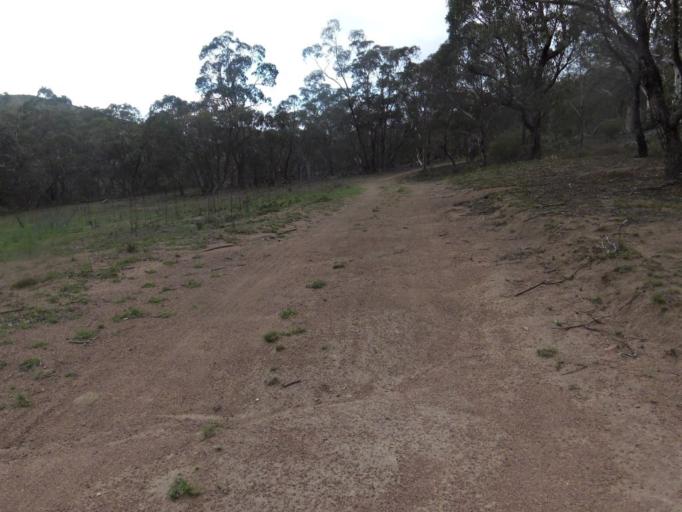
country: AU
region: Australian Capital Territory
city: Forrest
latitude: -35.3493
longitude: 149.1230
